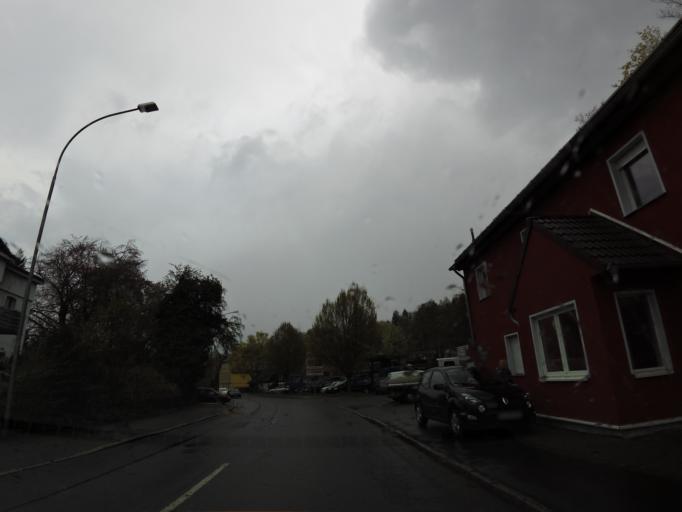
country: DE
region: Lower Saxony
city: Goslar
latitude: 51.8957
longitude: 10.4818
